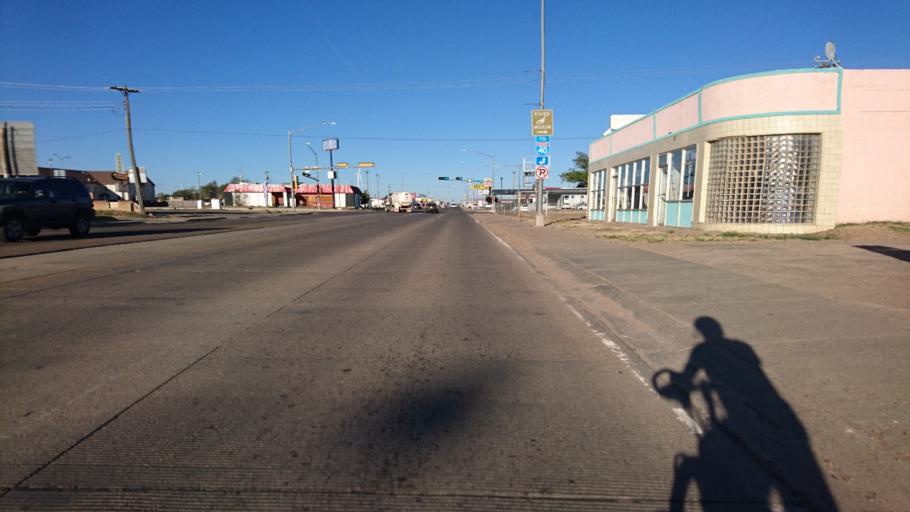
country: US
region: New Mexico
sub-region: Quay County
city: Tucumcari
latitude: 35.1719
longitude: -103.7238
